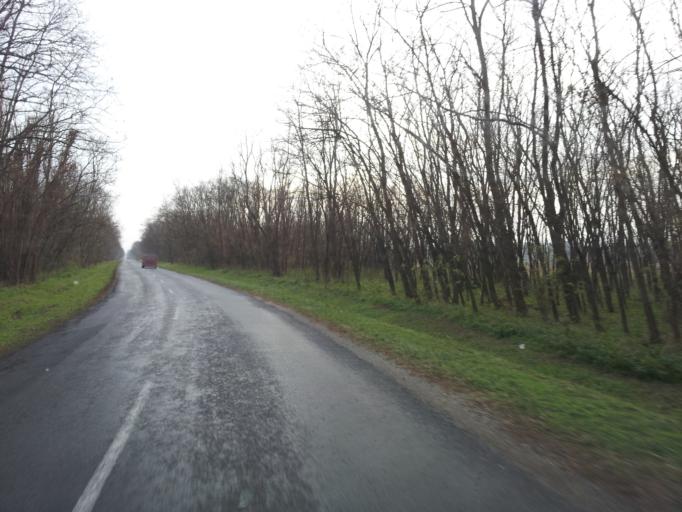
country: HU
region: Zala
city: Cserszegtomaj
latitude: 46.8602
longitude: 17.1994
